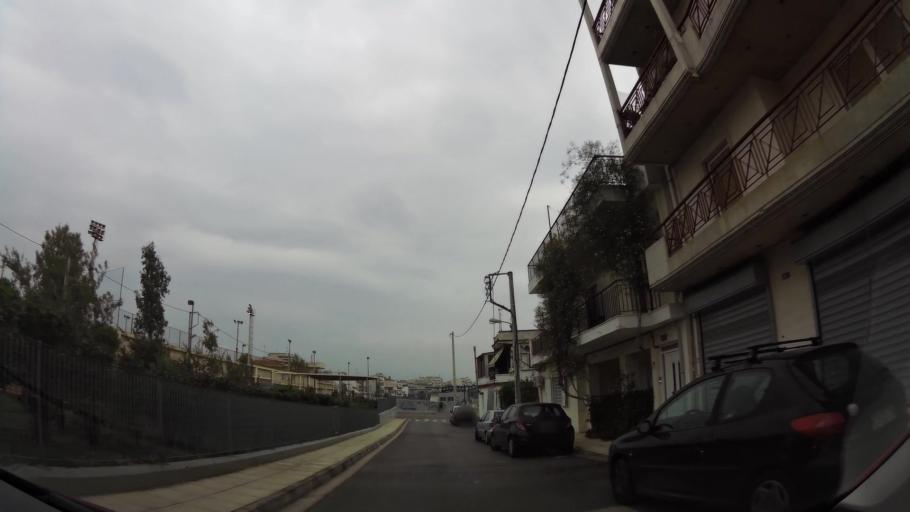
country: GR
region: Attica
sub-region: Nomarchia Athinas
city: Agioi Anargyroi
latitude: 38.0384
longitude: 23.7270
